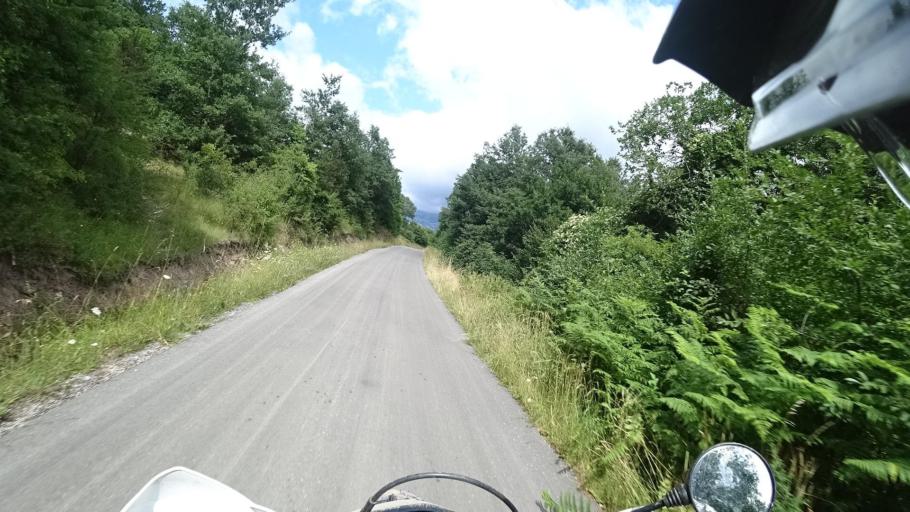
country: HR
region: Zadarska
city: Gracac
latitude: 44.5251
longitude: 15.7908
